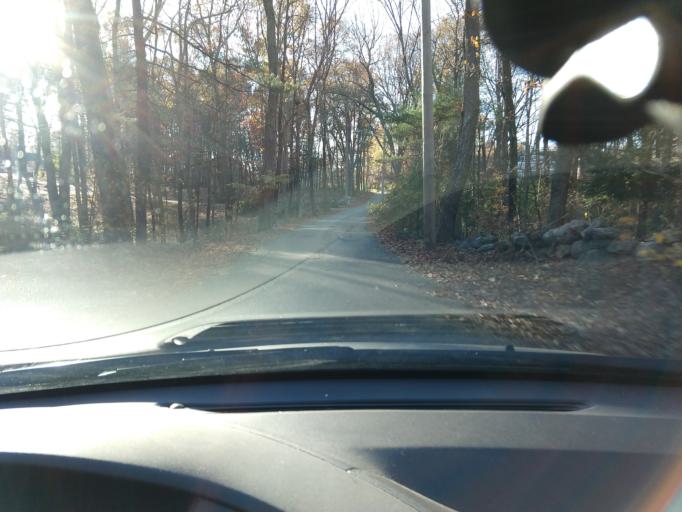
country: US
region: Massachusetts
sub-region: Middlesex County
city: Concord
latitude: 42.4889
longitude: -71.3303
